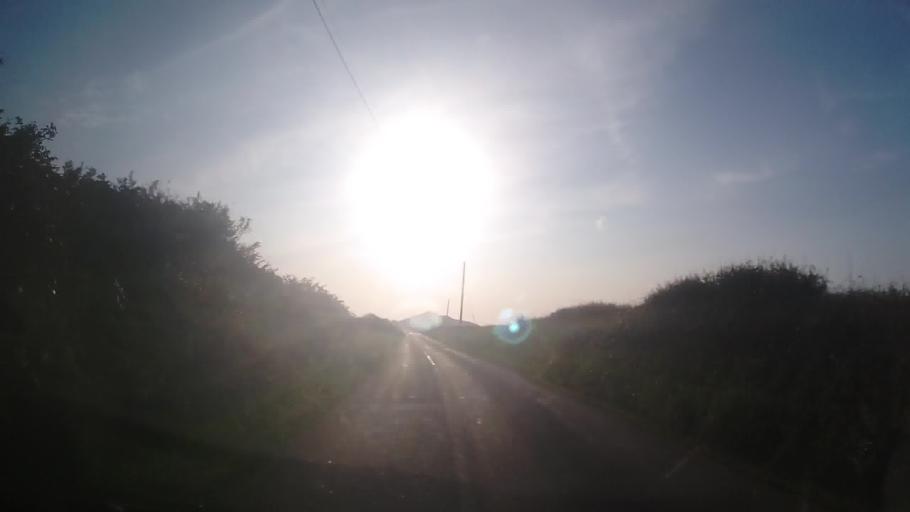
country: GB
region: Wales
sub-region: Pembrokeshire
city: Llanrhian
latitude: 51.9222
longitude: -5.2156
